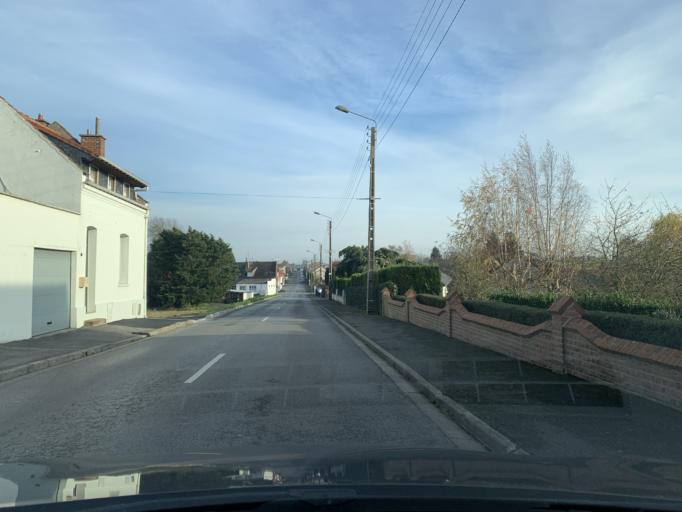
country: FR
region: Nord-Pas-de-Calais
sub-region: Departement du Nord
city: Cambrai
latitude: 50.1601
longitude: 3.2326
